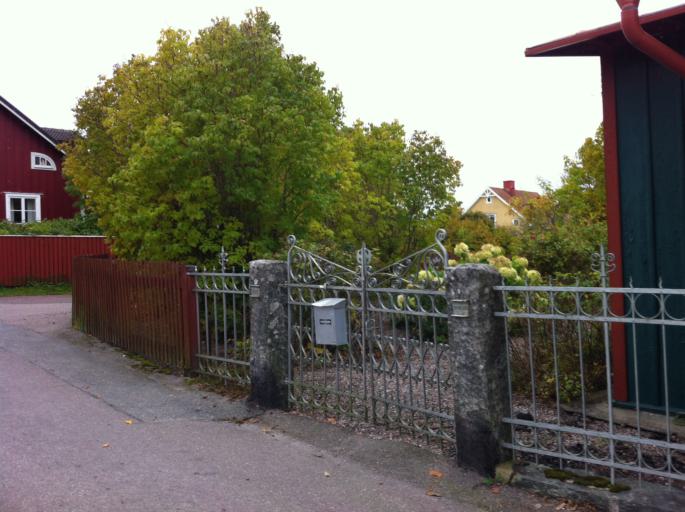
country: SE
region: Uppsala
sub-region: Osthammars Kommun
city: Oregrund
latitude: 60.3386
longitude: 18.4380
